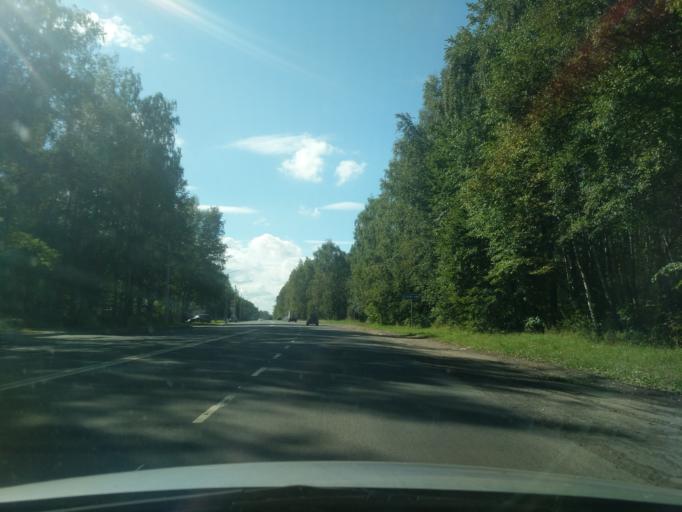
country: RU
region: Kostroma
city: Oktyabr'skiy
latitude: 57.7835
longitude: 41.0109
